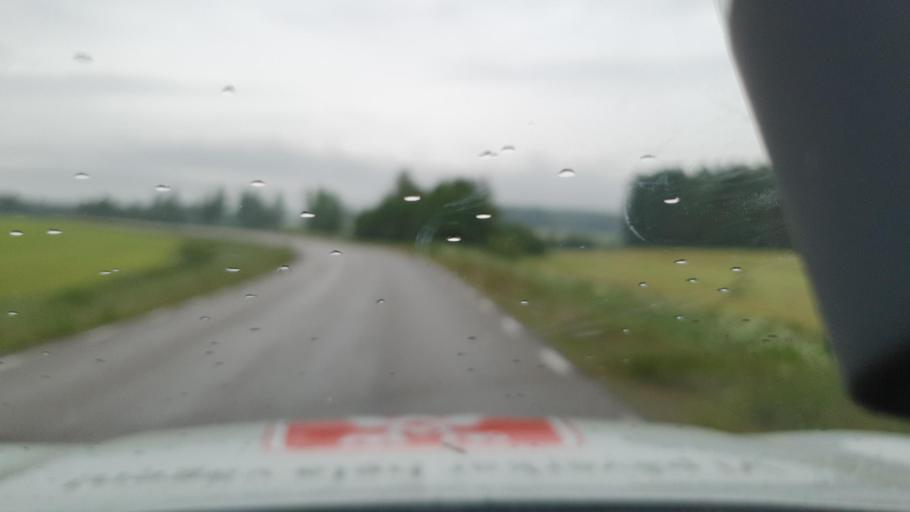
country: SE
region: Vaesterbotten
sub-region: Vannas Kommun
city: Vaennaes
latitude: 63.7886
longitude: 19.5722
